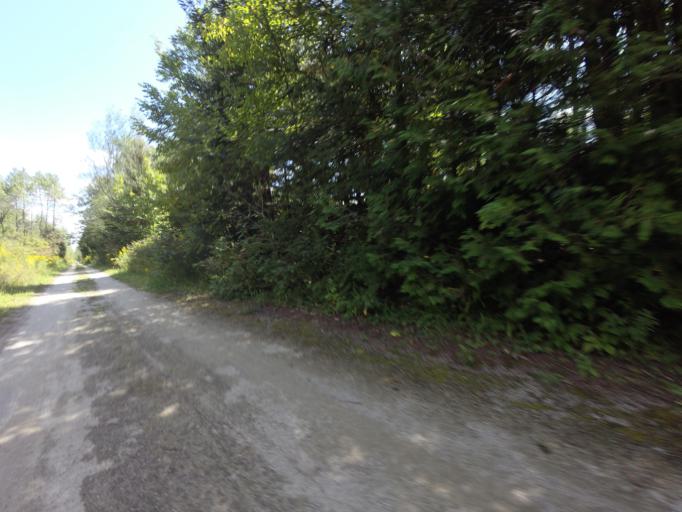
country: CA
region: Ontario
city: Orangeville
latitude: 43.7787
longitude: -80.1230
